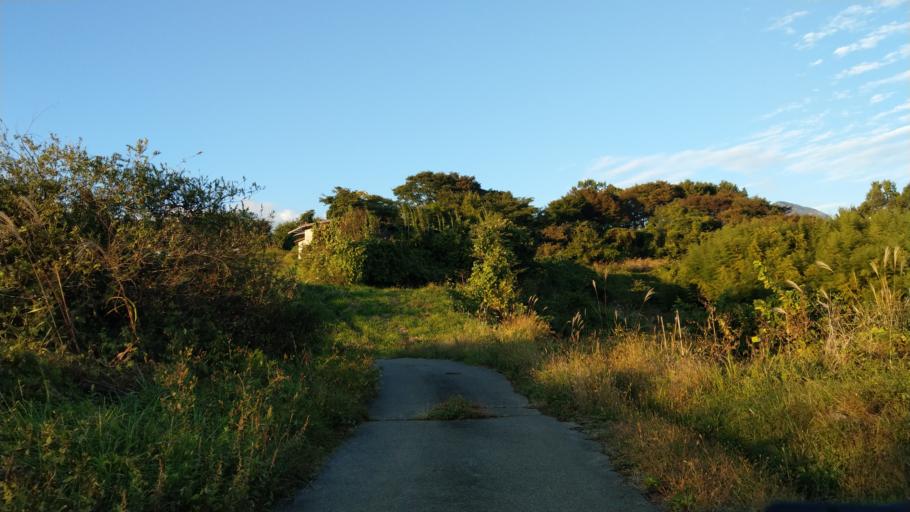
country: JP
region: Nagano
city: Komoro
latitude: 36.3459
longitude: 138.4262
